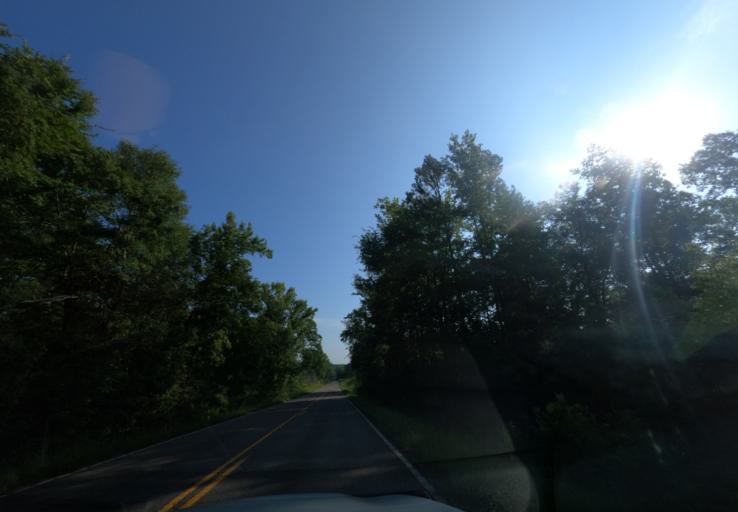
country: US
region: South Carolina
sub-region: Edgefield County
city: Edgefield
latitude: 33.7463
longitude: -81.9601
